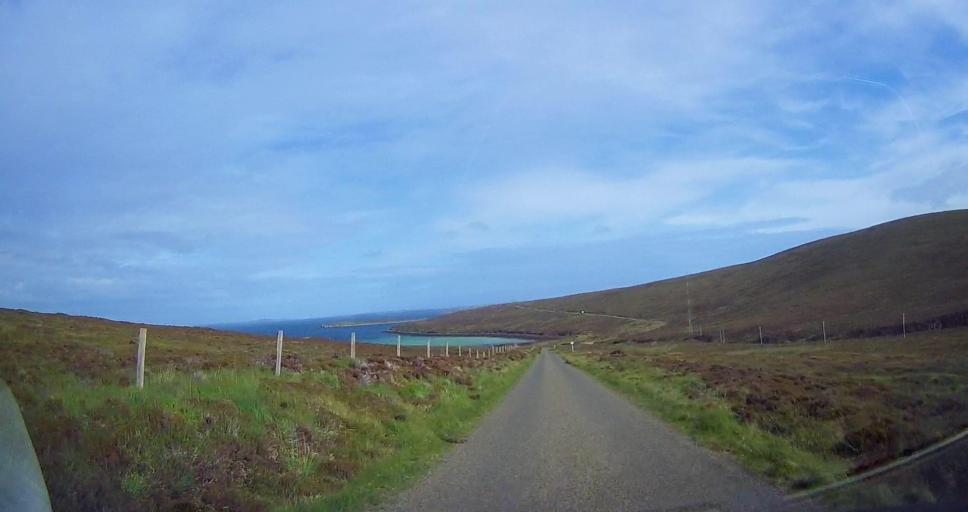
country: GB
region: Scotland
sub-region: Orkney Islands
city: Stromness
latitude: 58.8731
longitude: -3.2396
